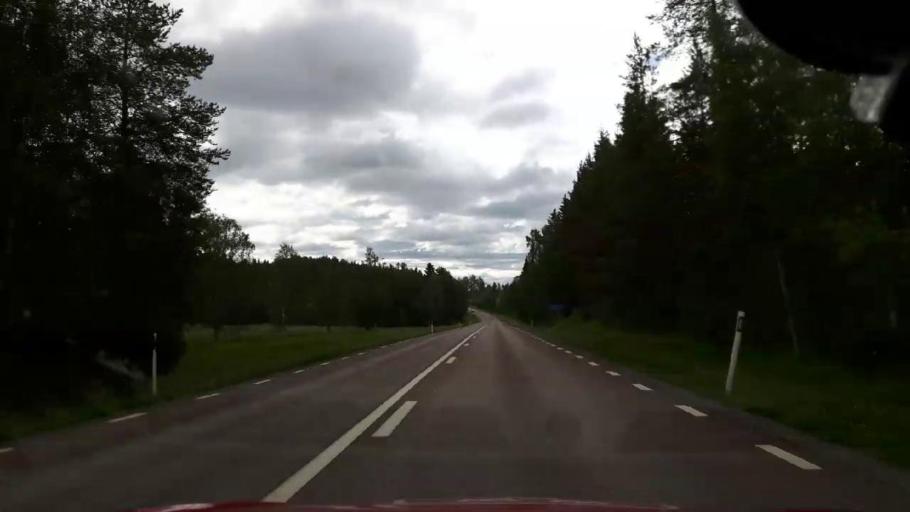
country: SE
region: Jaemtland
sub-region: OEstersunds Kommun
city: Brunflo
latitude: 63.0243
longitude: 14.9198
